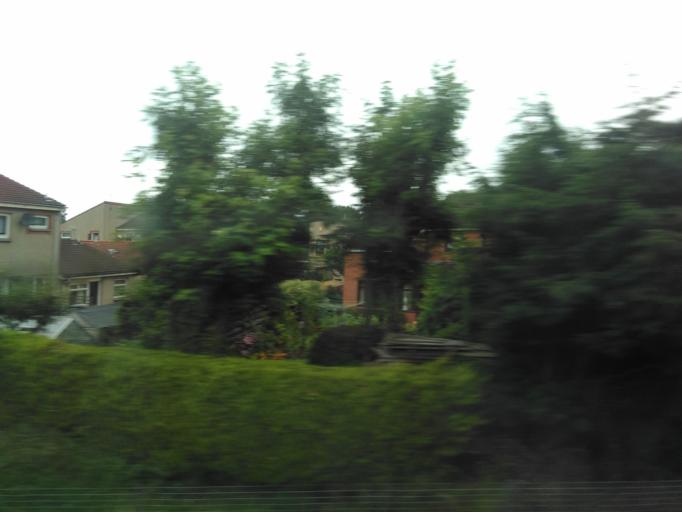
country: GB
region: Scotland
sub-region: East Lothian
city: Musselburgh
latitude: 55.9310
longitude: -3.0661
